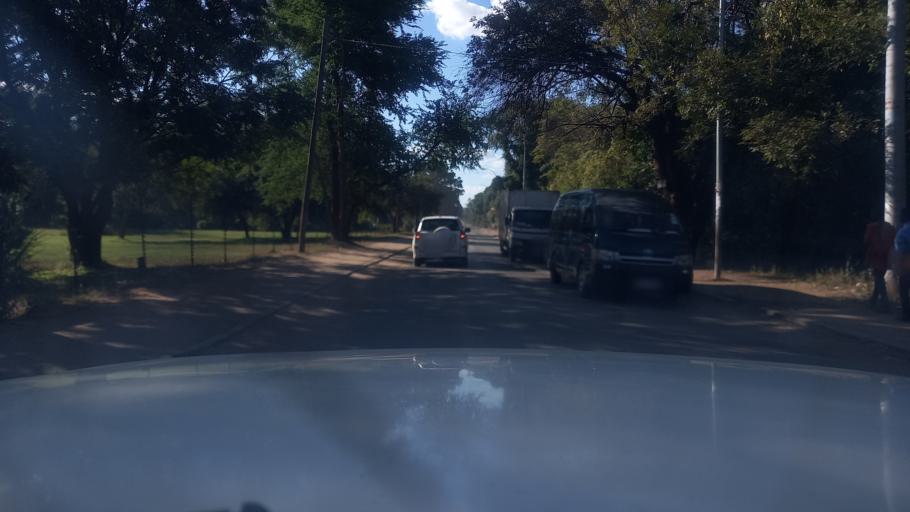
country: ZM
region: Southern
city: Livingstone
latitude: -17.8642
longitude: 25.8552
